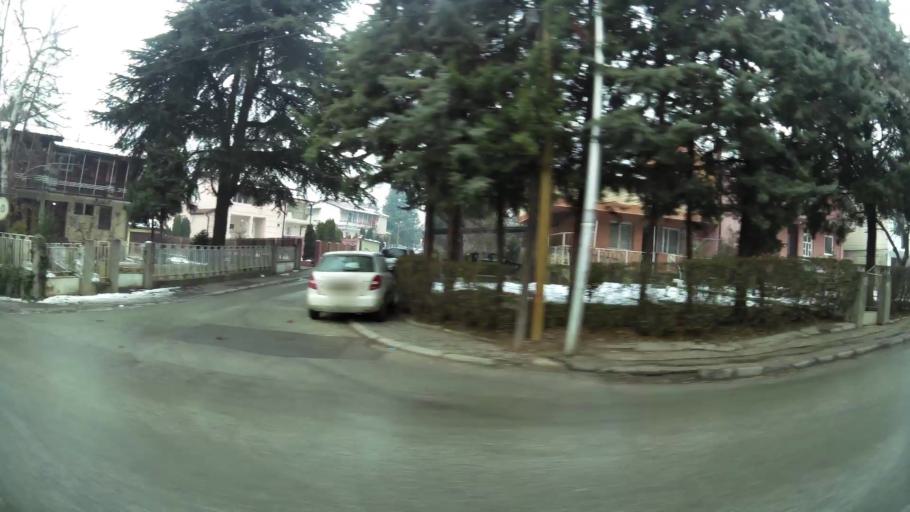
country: MK
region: Cair
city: Cair
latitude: 42.0182
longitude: 21.4528
